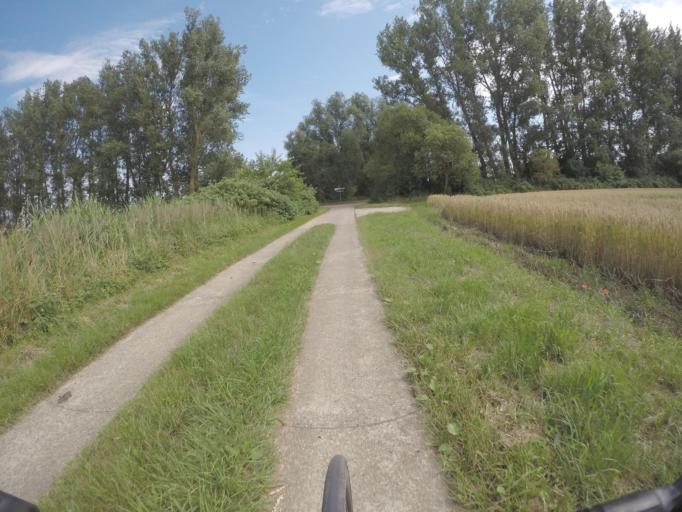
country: DE
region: Mecklenburg-Vorpommern
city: Altefahr
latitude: 54.3666
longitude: 13.1490
